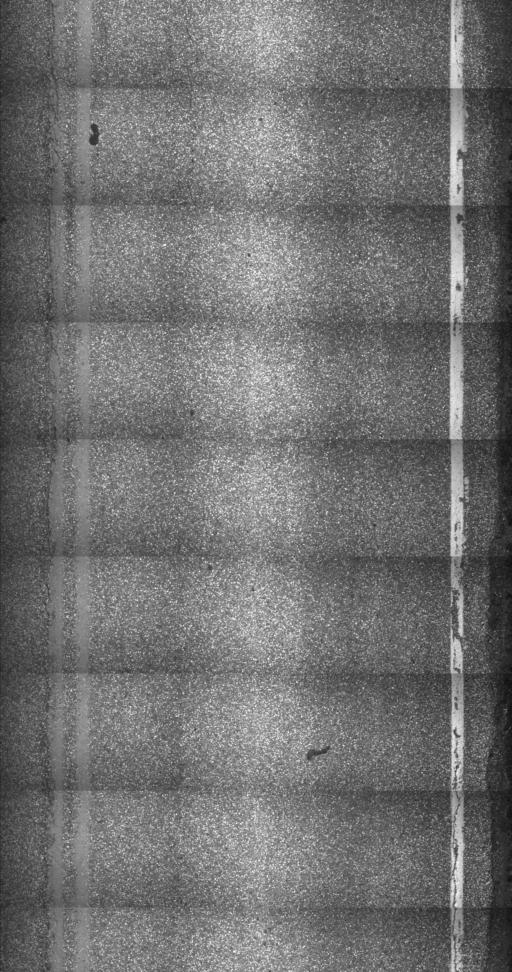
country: US
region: Vermont
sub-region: Franklin County
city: Saint Albans
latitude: 44.8247
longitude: -73.0896
